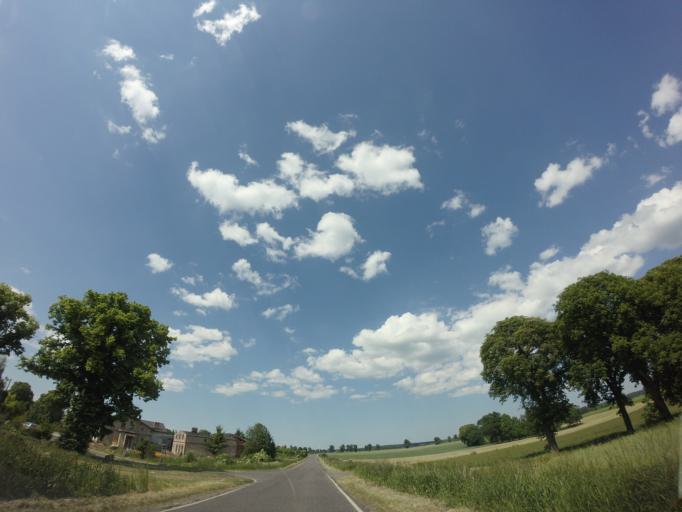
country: PL
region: West Pomeranian Voivodeship
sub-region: Powiat stargardzki
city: Dolice
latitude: 53.1447
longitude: 15.2428
